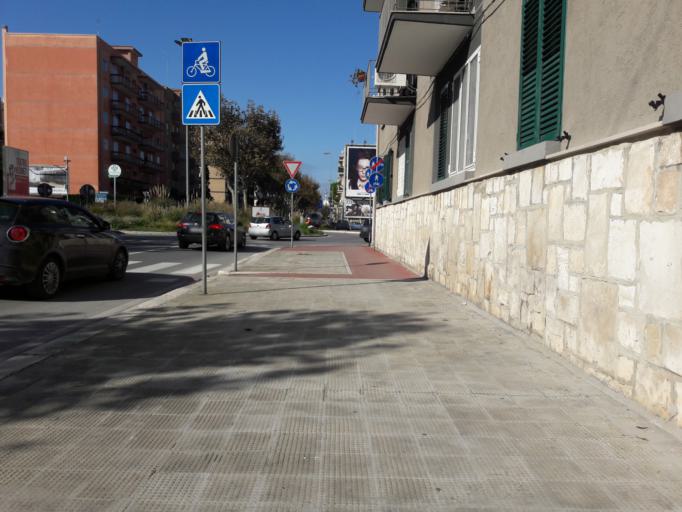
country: IT
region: Apulia
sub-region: Provincia di Bari
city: Bari
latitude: 41.1129
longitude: 16.8933
